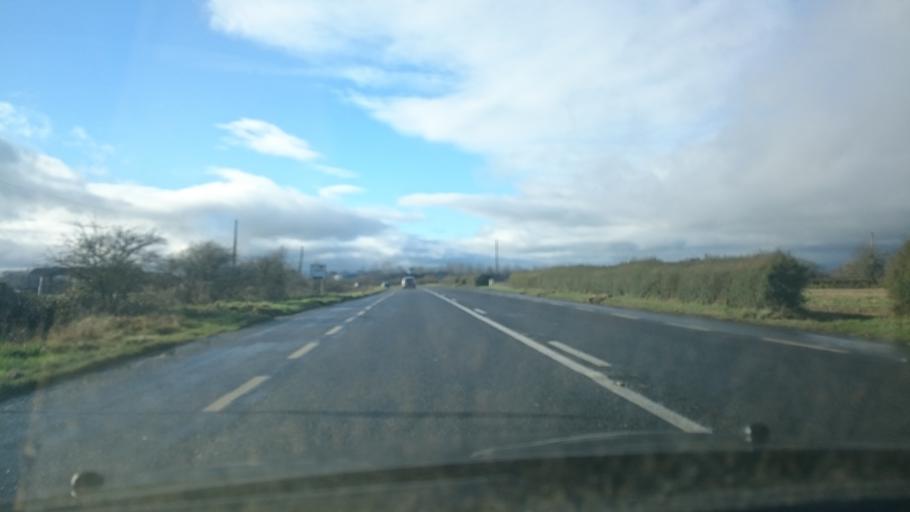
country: IE
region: Leinster
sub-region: Kilkenny
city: Callan
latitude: 52.5727
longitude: -7.3364
